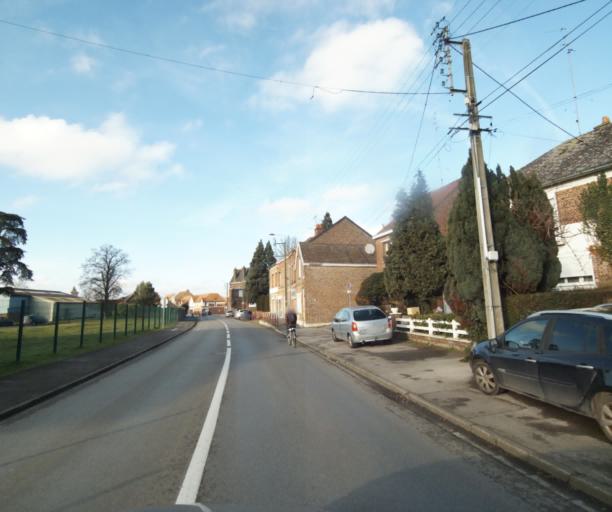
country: FR
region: Nord-Pas-de-Calais
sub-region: Departement du Nord
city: Marly
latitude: 50.3480
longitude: 3.5427
